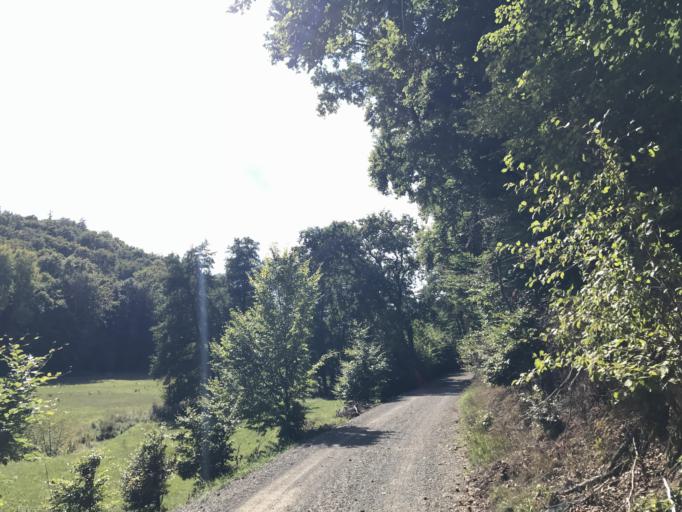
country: DE
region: Hesse
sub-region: Regierungsbezirk Kassel
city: Sachsenhausen
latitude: 51.2239
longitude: 9.0310
